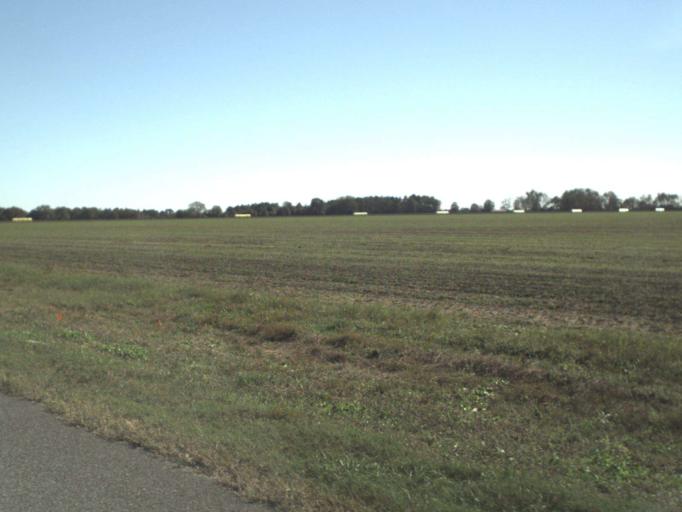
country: US
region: Florida
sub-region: Okaloosa County
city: Crestview
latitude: 30.8499
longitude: -86.7565
